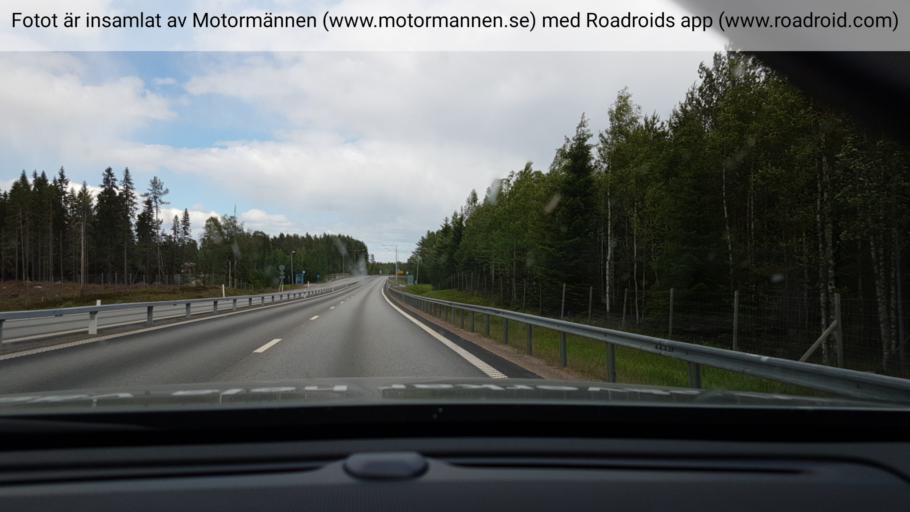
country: SE
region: Vaesterbotten
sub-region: Umea Kommun
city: Hoernefors
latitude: 63.6256
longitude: 19.8545
